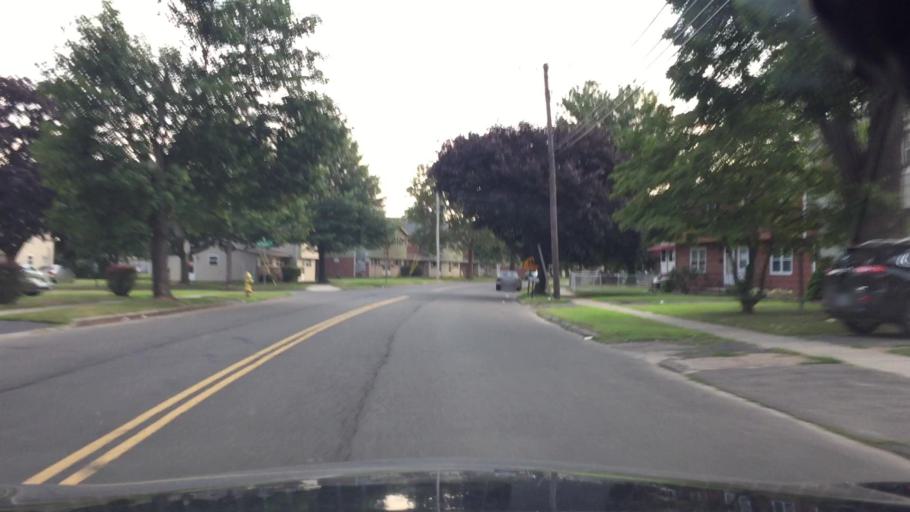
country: US
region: Connecticut
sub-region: Fairfield County
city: Stratford
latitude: 41.1755
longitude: -73.1329
